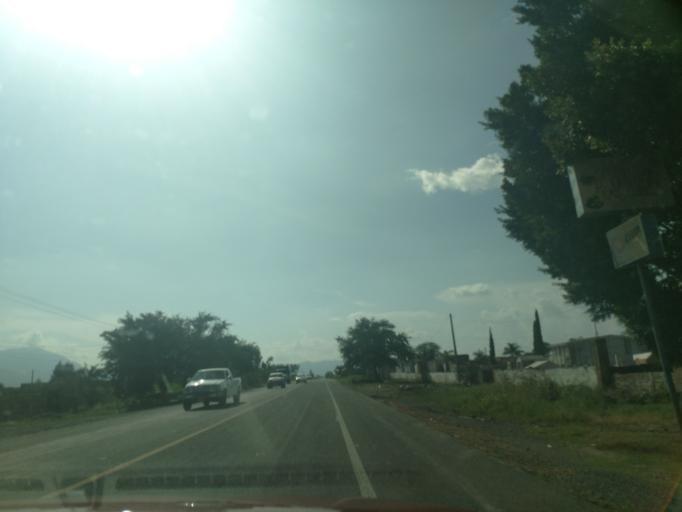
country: MX
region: Jalisco
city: Teuchitlan
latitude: 20.6815
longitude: -103.8517
